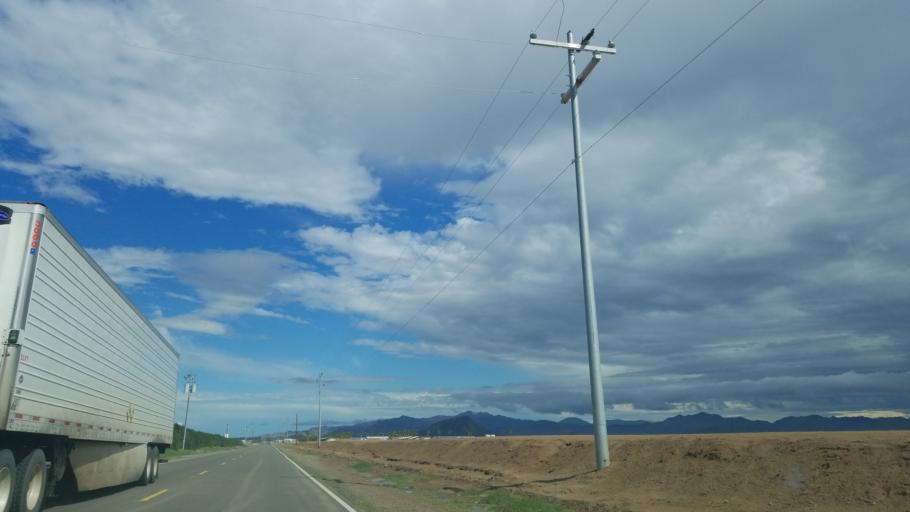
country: US
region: Arizona
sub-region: La Paz County
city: Salome
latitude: 33.6693
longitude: -113.7672
